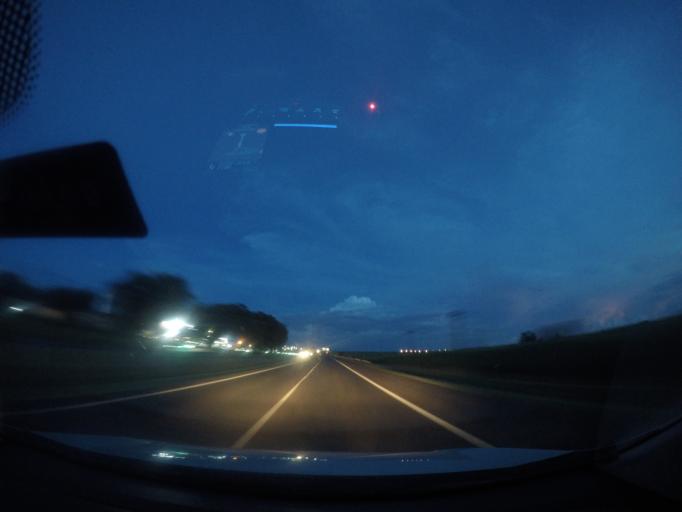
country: BR
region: Sao Paulo
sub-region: Cordeiropolis
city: Cordeiropolis
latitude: -22.4984
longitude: -47.4135
